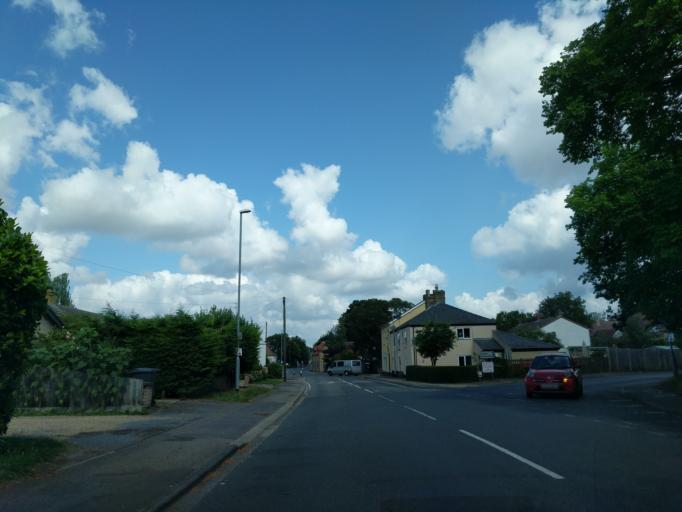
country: GB
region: England
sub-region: Suffolk
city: Exning
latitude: 52.3057
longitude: 0.3857
